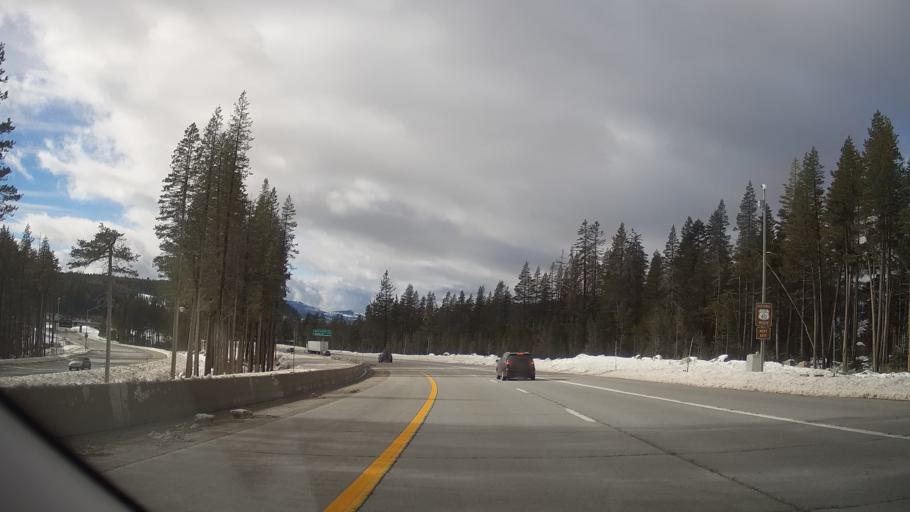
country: US
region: California
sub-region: Nevada County
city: Truckee
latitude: 39.3279
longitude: -120.3864
